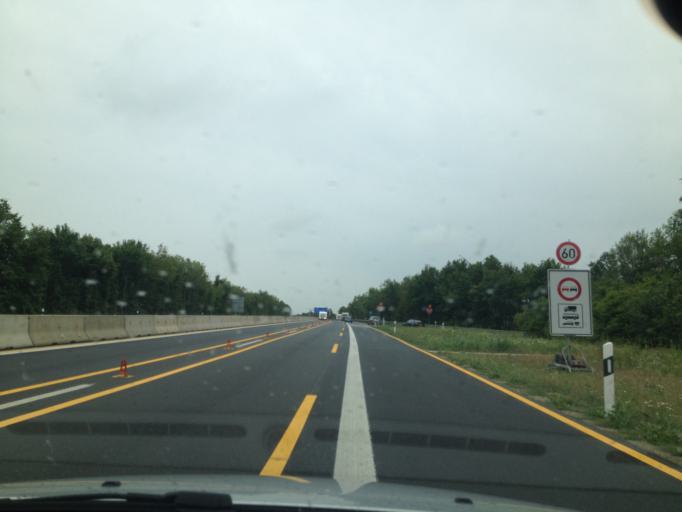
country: DE
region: Bavaria
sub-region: Regierungsbezirk Unterfranken
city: Biebelried
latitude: 49.7604
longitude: 10.1053
